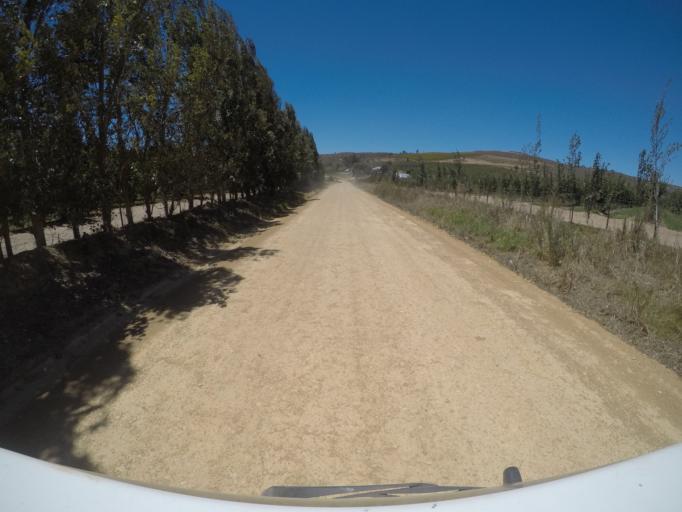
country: ZA
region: Western Cape
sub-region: Overberg District Municipality
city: Grabouw
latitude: -34.1135
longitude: 19.2185
